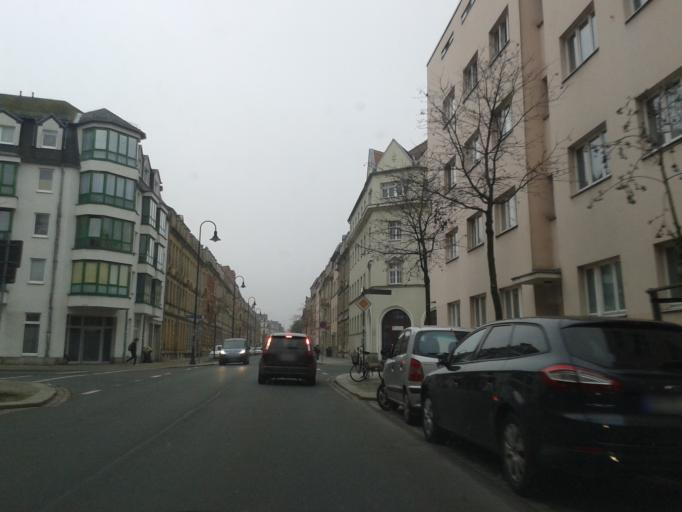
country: DE
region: Saxony
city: Dresden
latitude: 51.0803
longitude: 13.7200
